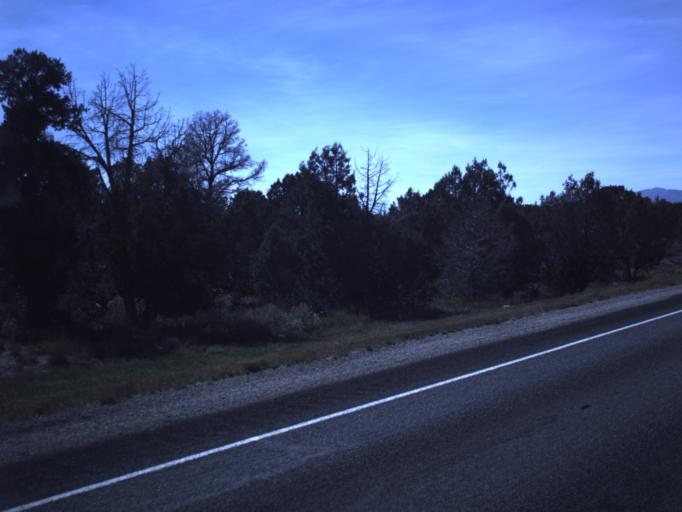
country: US
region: Colorado
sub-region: Dolores County
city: Dove Creek
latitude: 37.8291
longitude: -109.0858
